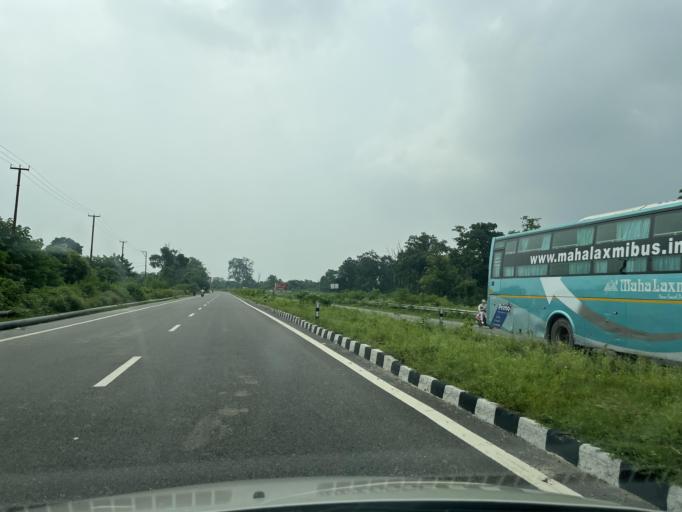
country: IN
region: Uttarakhand
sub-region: Dehradun
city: Raiwala
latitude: 30.0606
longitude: 78.2128
